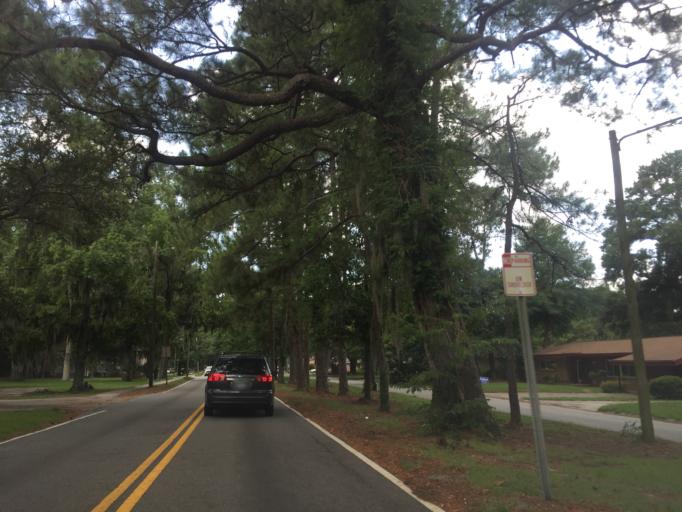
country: US
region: Georgia
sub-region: Chatham County
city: Savannah
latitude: 32.0352
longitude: -81.1087
